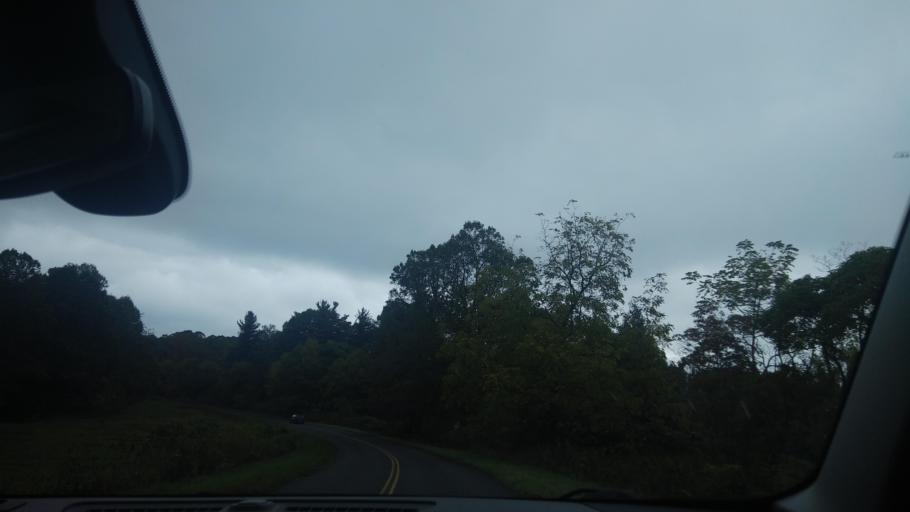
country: US
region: Virginia
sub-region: Carroll County
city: Cana
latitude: 36.6703
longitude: -80.6334
